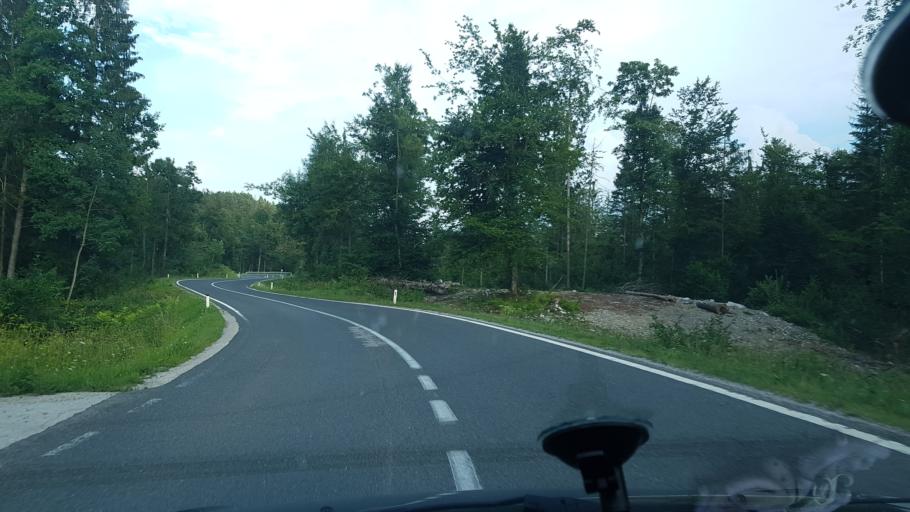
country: SI
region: Logatec
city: Logatec
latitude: 45.9157
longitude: 14.1514
